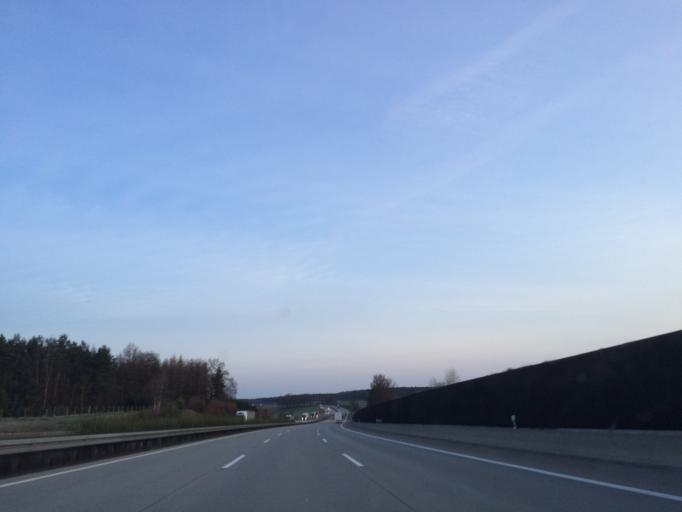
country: DE
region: Thuringia
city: Tautendorf
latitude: 50.8214
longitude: 11.8841
